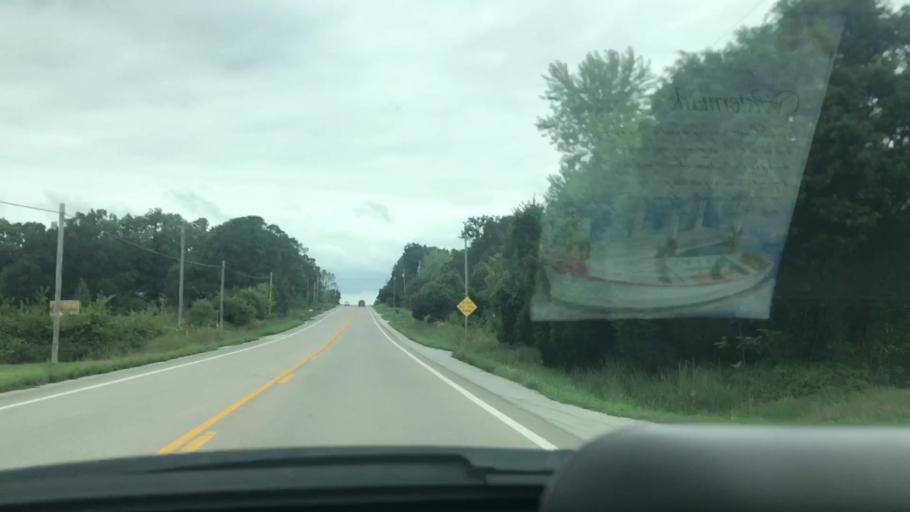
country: US
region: Missouri
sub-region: Dallas County
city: Buffalo
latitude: 37.7001
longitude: -93.1066
